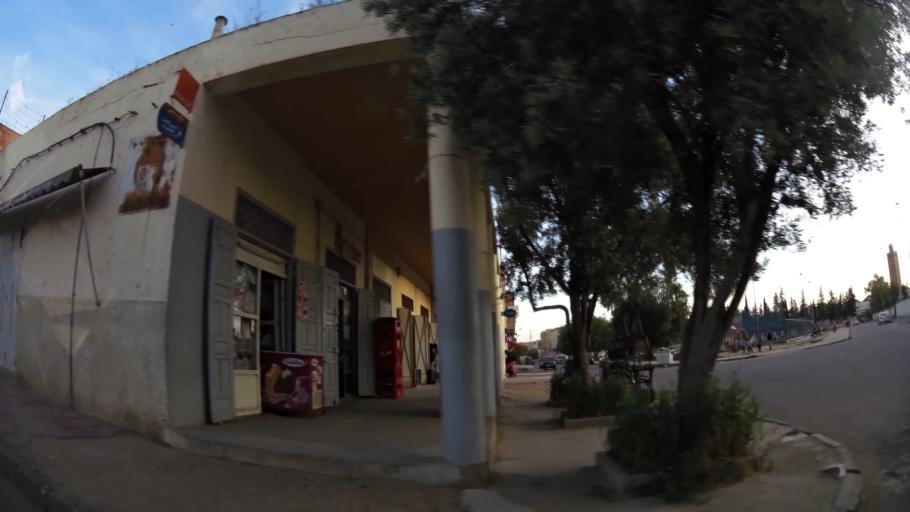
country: MA
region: Oriental
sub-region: Oujda-Angad
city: Oujda
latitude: 34.6794
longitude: -1.8846
